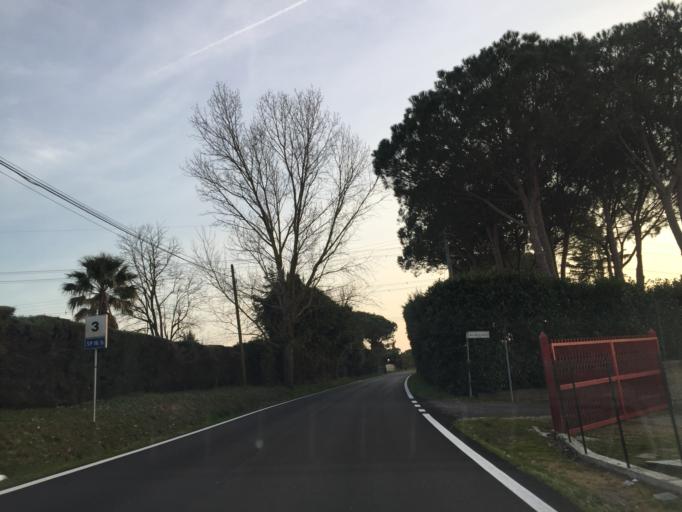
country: IT
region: Latium
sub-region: Citta metropolitana di Roma Capitale
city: Mazzano Romano
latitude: 42.1802
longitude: 12.3626
